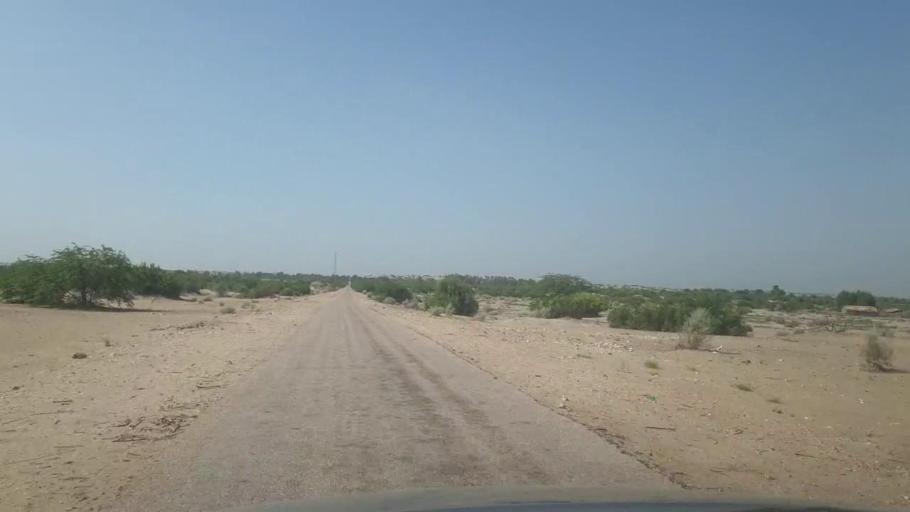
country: PK
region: Sindh
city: Rohri
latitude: 27.4204
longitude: 69.0798
